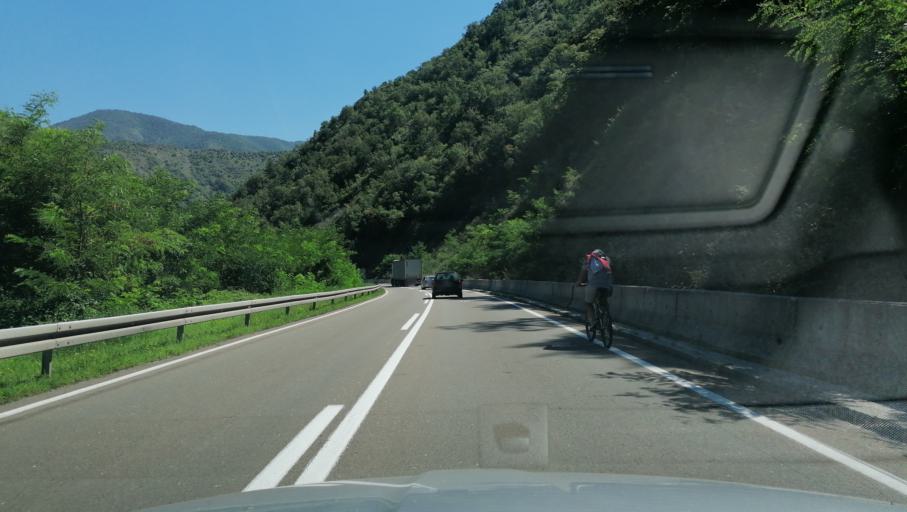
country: RS
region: Central Serbia
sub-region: Raski Okrug
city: Kraljevo
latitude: 43.5612
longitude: 20.6092
